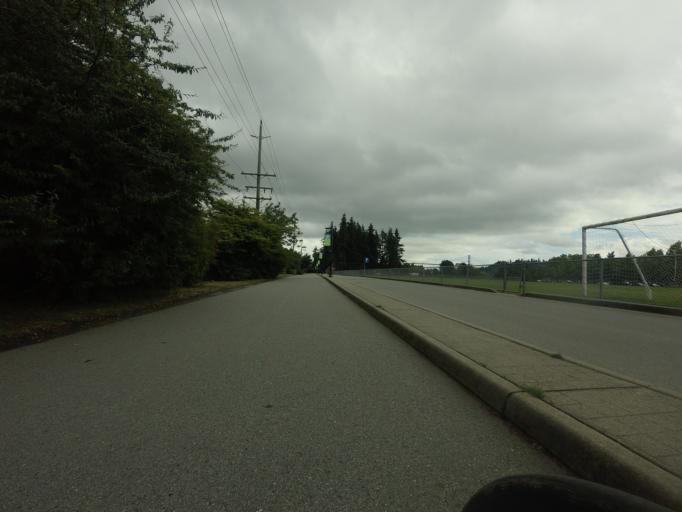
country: CA
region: British Columbia
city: West Vancouver
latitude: 49.3261
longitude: -123.1502
